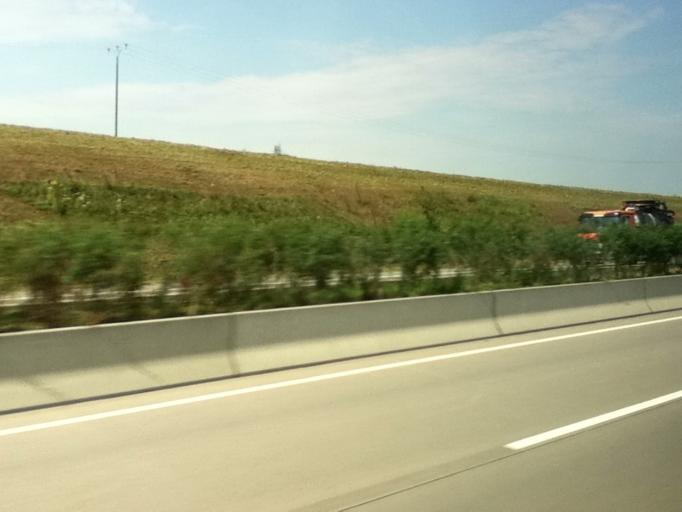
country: DE
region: Thuringia
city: Nobdenitz
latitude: 50.8638
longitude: 12.2855
